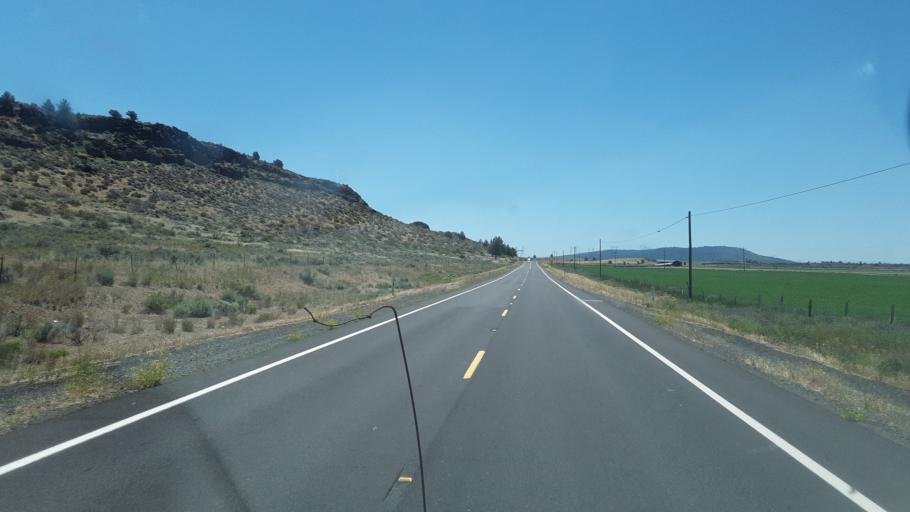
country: US
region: California
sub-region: Siskiyou County
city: Tulelake
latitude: 41.7304
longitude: -121.2961
